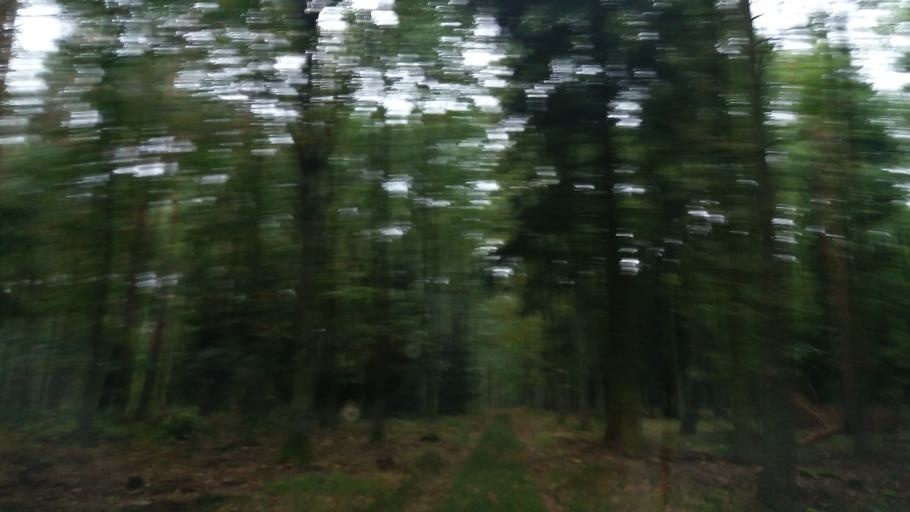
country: PL
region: West Pomeranian Voivodeship
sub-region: Powiat choszczenski
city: Pelczyce
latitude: 53.0737
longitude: 15.2871
